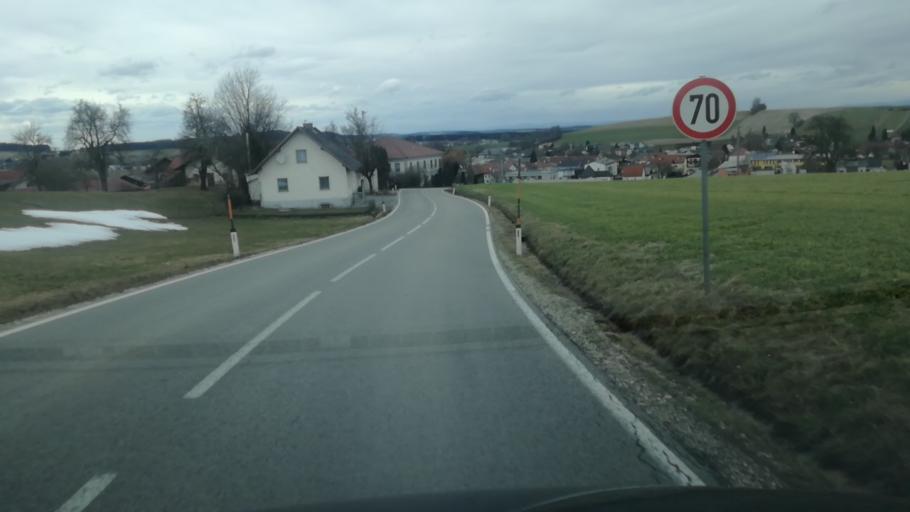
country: AT
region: Upper Austria
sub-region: Politischer Bezirk Ried im Innkreis
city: Waldzell
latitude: 48.1351
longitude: 13.4865
